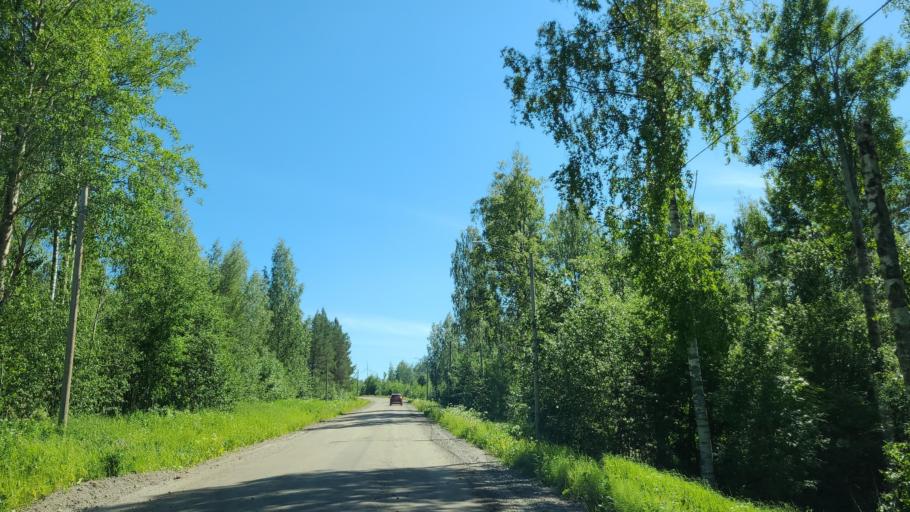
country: SE
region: Vaesterbotten
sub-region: Bjurholms Kommun
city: Bjurholm
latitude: 63.6900
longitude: 18.9575
